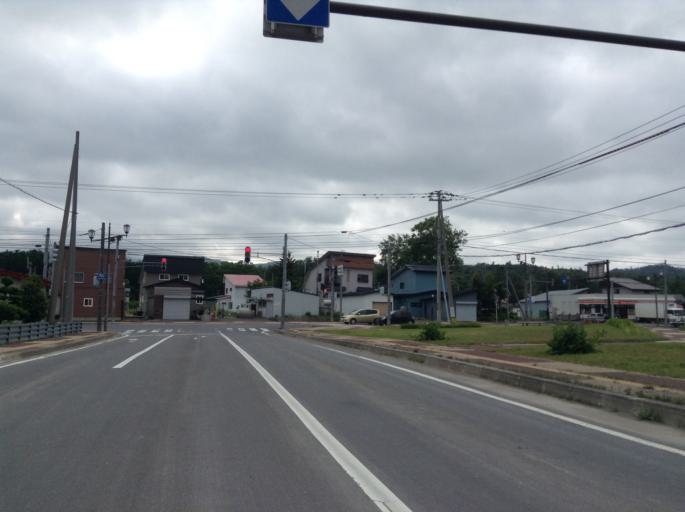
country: JP
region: Hokkaido
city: Nayoro
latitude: 44.8174
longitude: 142.0742
